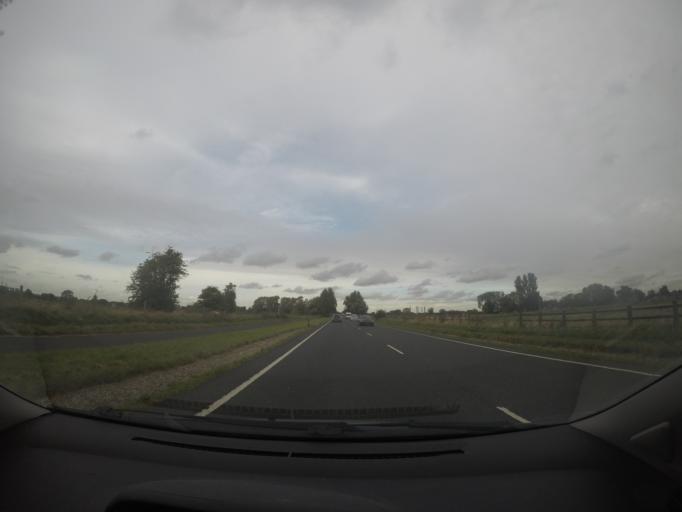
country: GB
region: England
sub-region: North Yorkshire
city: Riccall
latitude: 53.8237
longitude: -1.0479
